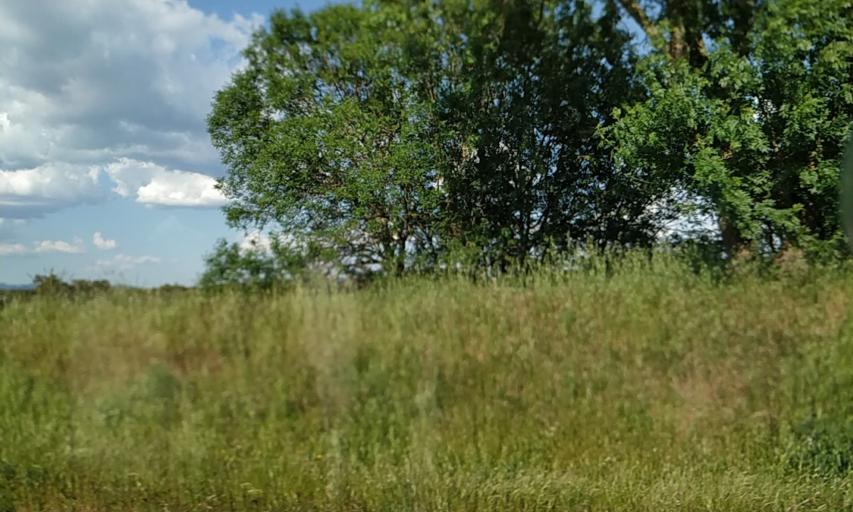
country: PT
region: Portalegre
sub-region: Portalegre
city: Urra
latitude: 39.1616
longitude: -7.4540
